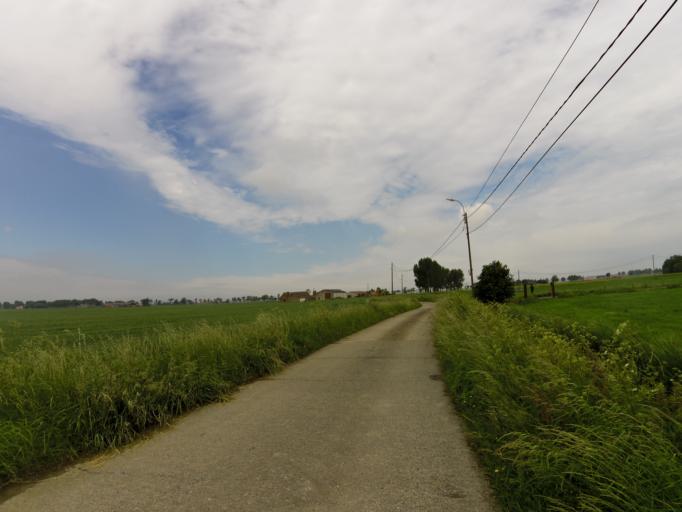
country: BE
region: Flanders
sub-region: Provincie West-Vlaanderen
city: Middelkerke
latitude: 51.1532
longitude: 2.8235
